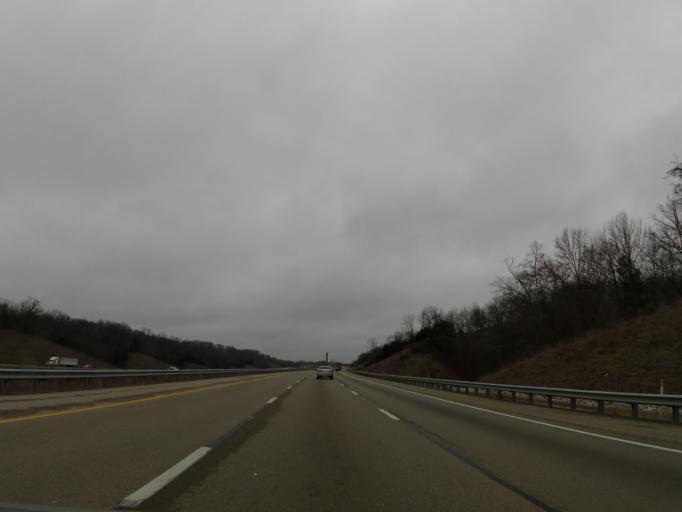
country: US
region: Kentucky
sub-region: Grant County
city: Williamstown
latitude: 38.5388
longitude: -84.5929
